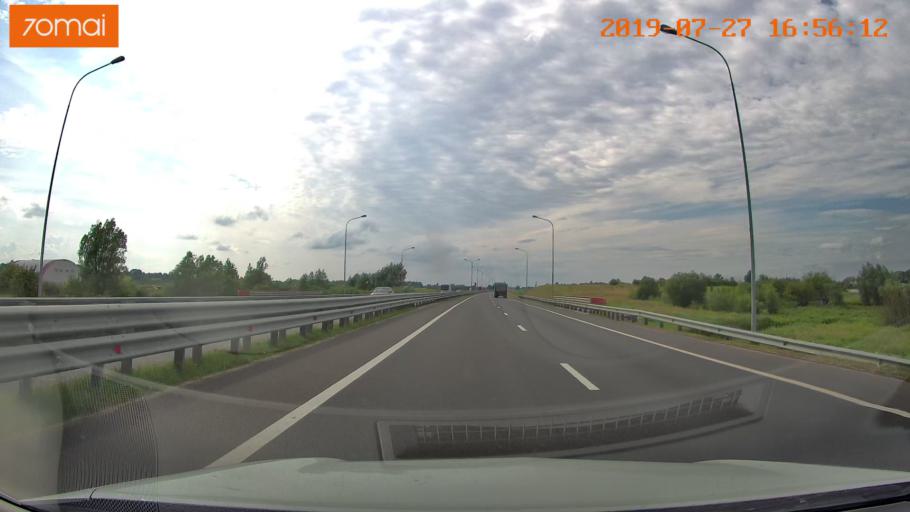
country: RU
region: Kaliningrad
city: Bol'shoe Isakovo
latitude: 54.6935
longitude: 20.7471
